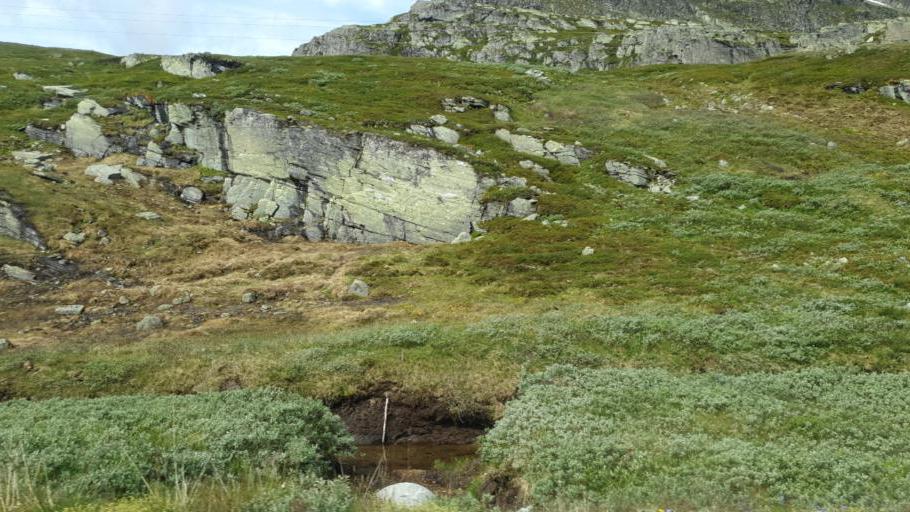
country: NO
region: Oppland
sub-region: Vestre Slidre
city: Slidre
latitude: 61.2912
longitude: 8.8137
